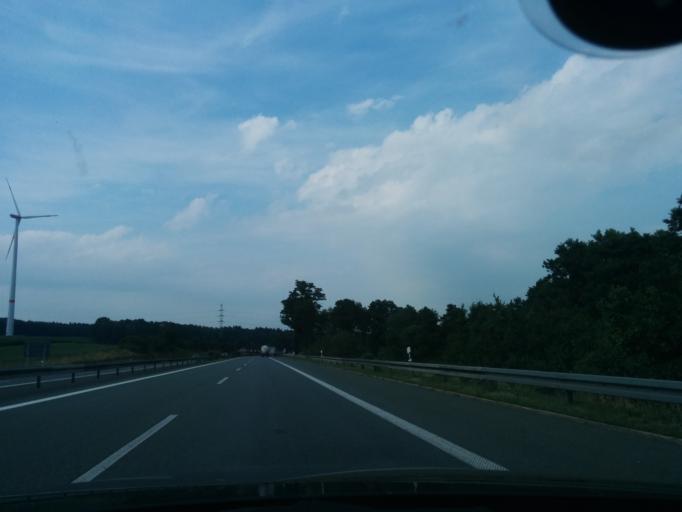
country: DE
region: Saxony
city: Treuen
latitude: 50.5660
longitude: 12.2847
